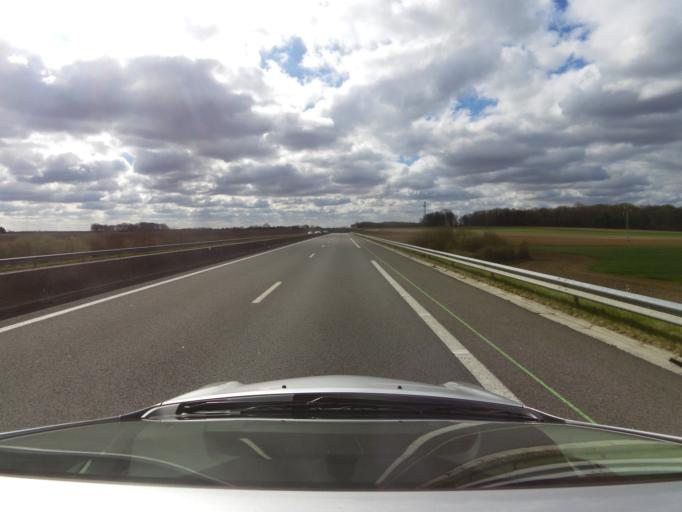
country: FR
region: Picardie
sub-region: Departement de la Somme
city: Rue
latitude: 50.2840
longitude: 1.7323
